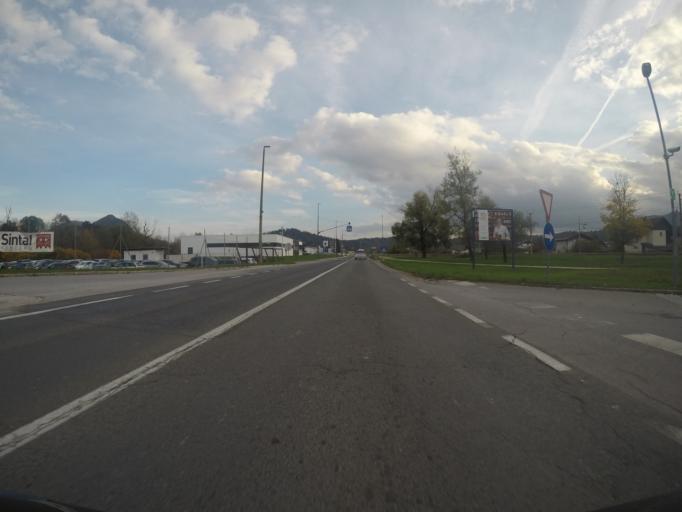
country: SI
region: Medvode
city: Medvode
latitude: 46.1367
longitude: 14.4167
